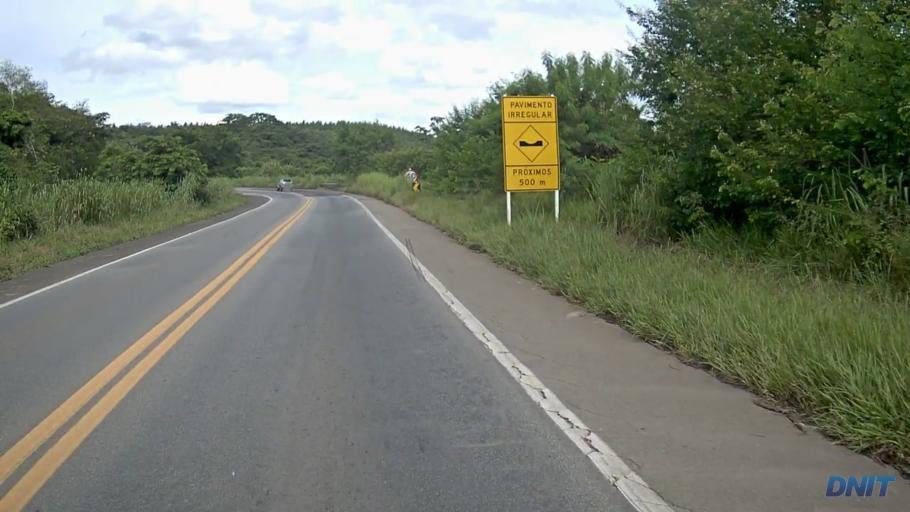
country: BR
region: Minas Gerais
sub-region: Ipaba
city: Ipaba
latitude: -19.3599
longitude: -42.4400
